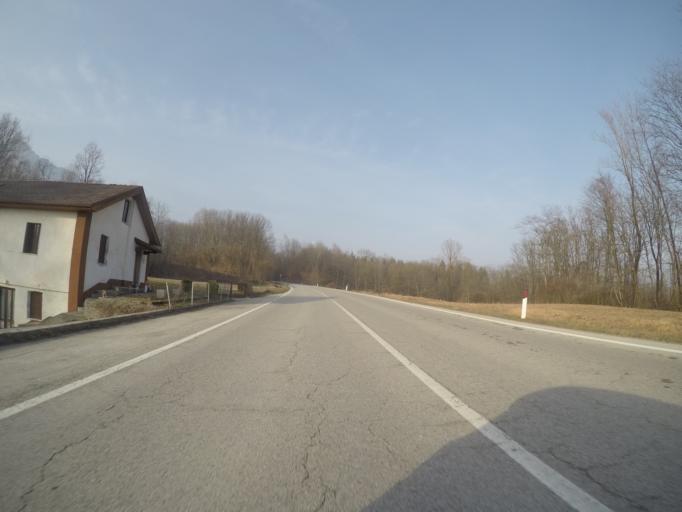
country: IT
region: Veneto
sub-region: Provincia di Belluno
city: Sedico
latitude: 46.1172
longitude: 12.0758
